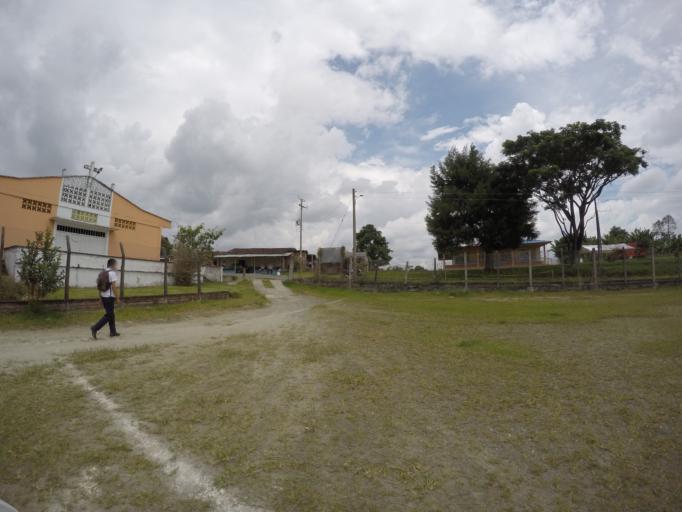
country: CO
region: Quindio
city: Quimbaya
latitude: 4.6139
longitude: -75.7054
